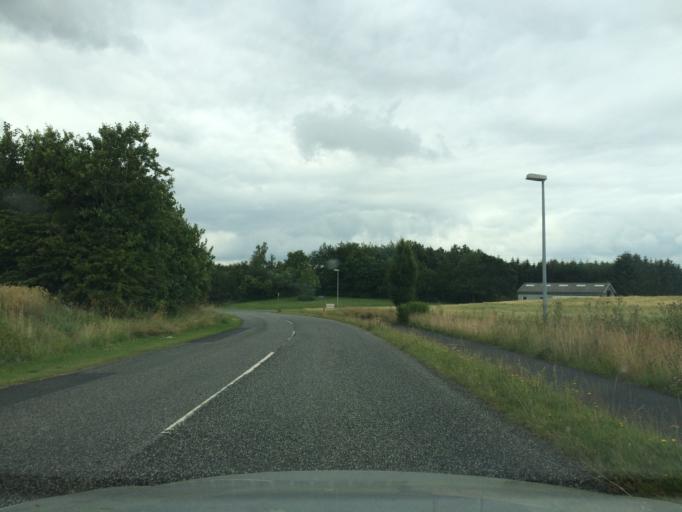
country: DK
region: Central Jutland
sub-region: Favrskov Kommune
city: Hammel
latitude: 56.2185
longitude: 9.7429
